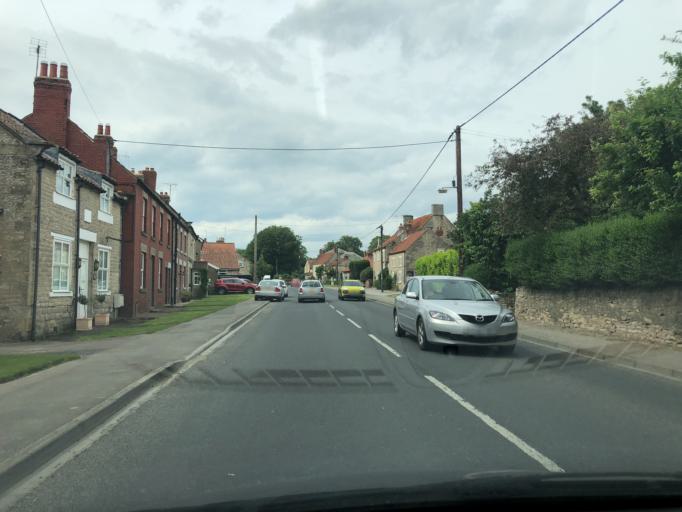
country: GB
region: England
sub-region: North Yorkshire
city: Pickering
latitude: 54.2564
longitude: -0.7981
